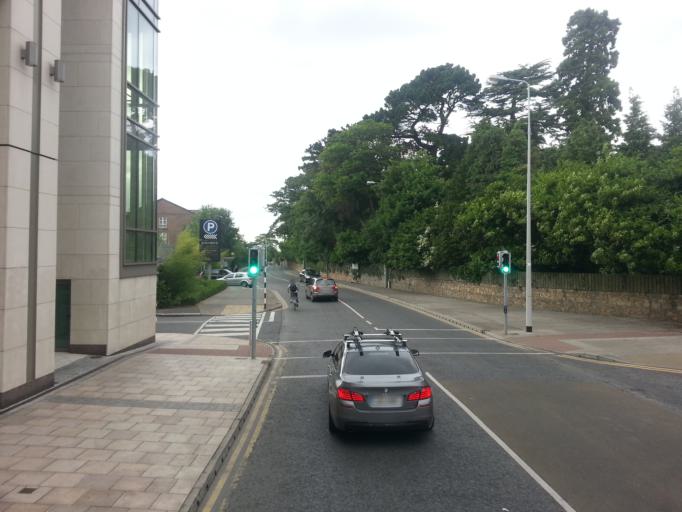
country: IE
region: Leinster
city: Balally
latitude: 53.2866
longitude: -6.2392
